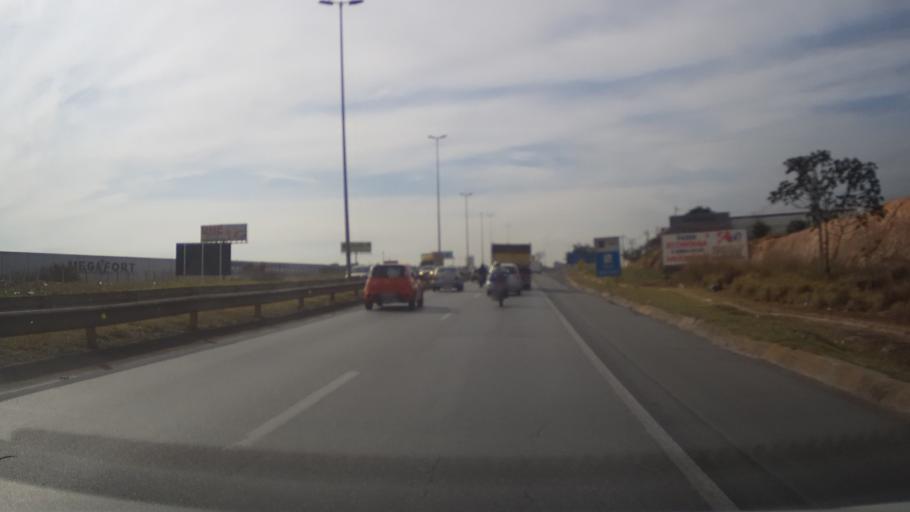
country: BR
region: Minas Gerais
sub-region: Contagem
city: Contagem
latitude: -19.9104
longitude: -44.0431
